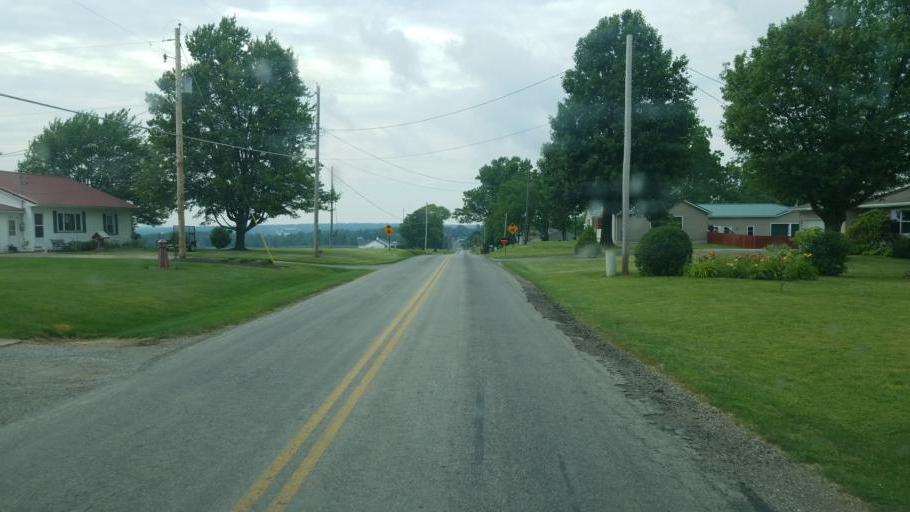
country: US
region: Ohio
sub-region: Wayne County
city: Wooster
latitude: 40.7817
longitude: -81.8988
